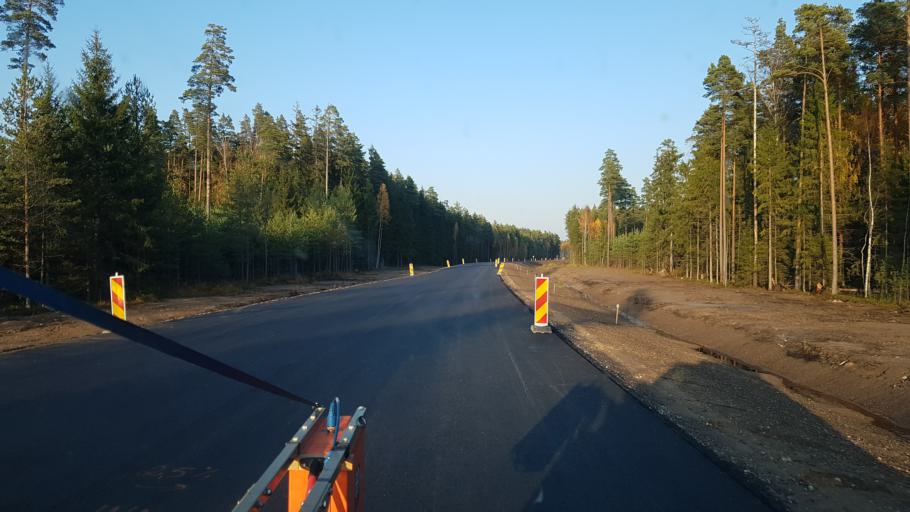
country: EE
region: Polvamaa
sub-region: Polva linn
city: Polva
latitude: 57.9339
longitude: 27.1874
